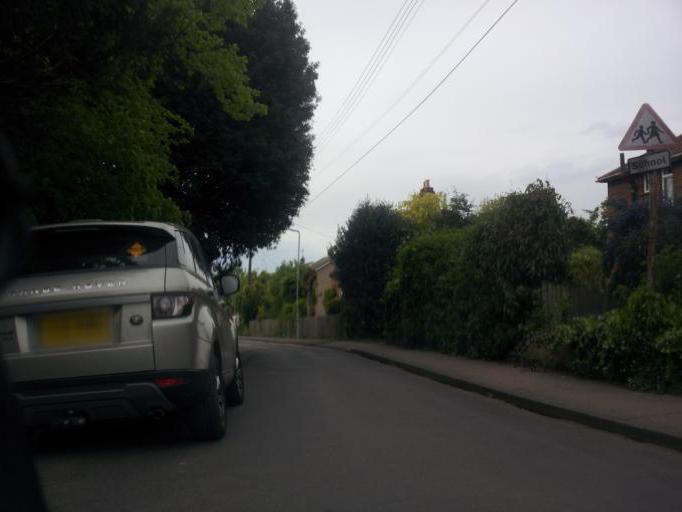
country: GB
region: England
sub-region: Kent
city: Faversham
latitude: 51.3197
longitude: 0.8849
